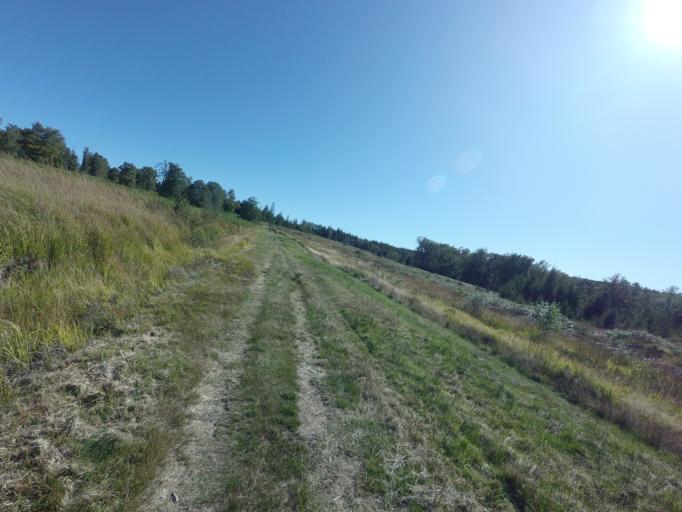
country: DE
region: North Rhine-Westphalia
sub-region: Regierungsbezirk Koln
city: Roetgen
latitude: 50.5930
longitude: 6.1468
